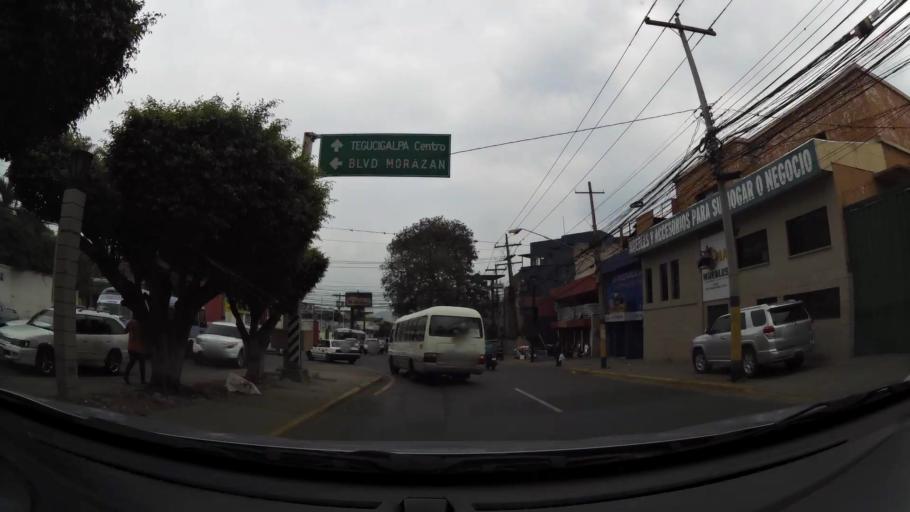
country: HN
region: Francisco Morazan
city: Tegucigalpa
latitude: 14.1031
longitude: -87.1873
